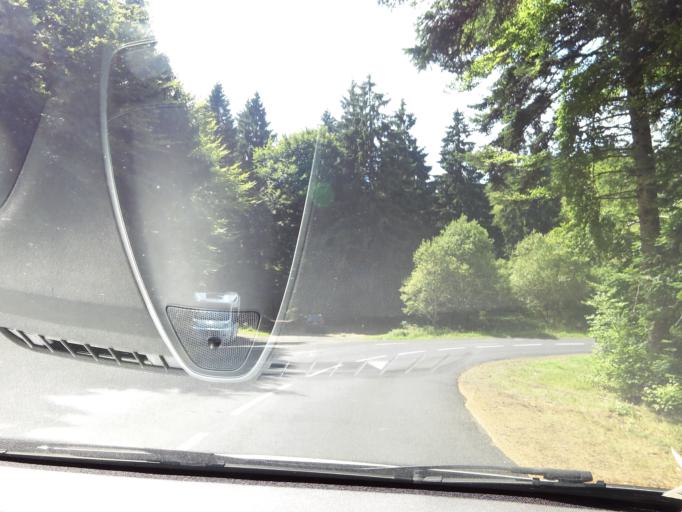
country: FR
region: Auvergne
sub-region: Departement du Puy-de-Dome
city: Orcines
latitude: 45.7614
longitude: 2.9510
